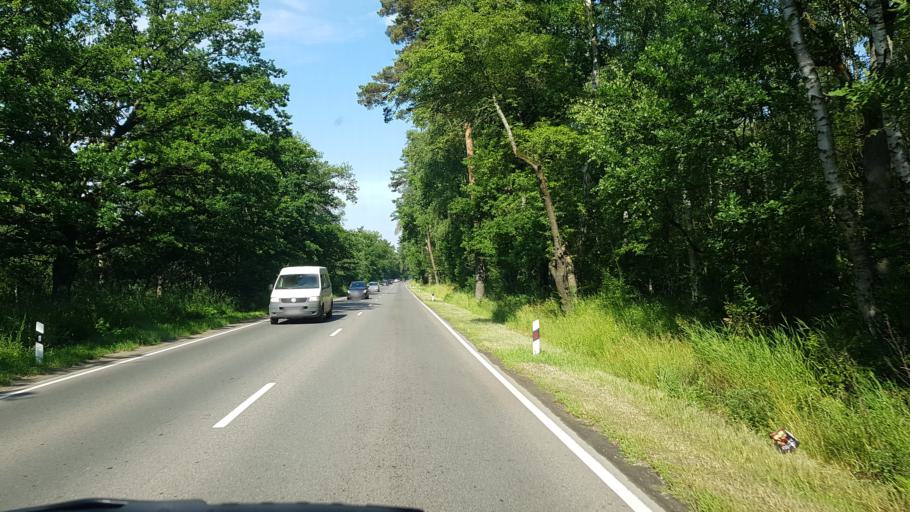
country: RU
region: Kaliningrad
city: Vzmorye
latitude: 54.7047
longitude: 20.2949
